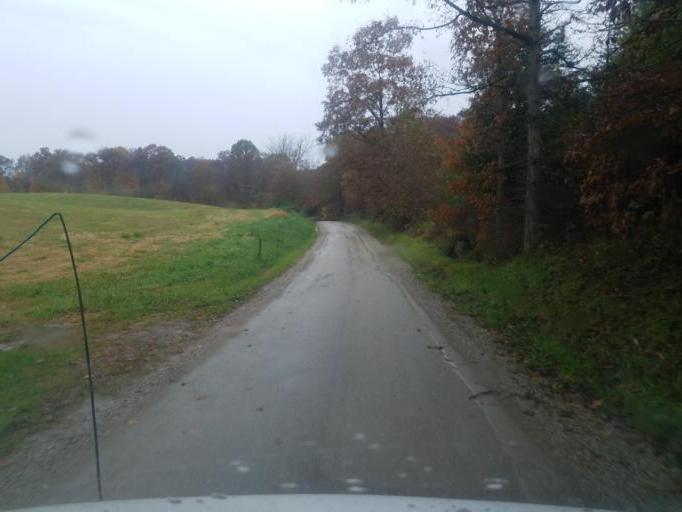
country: US
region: Ohio
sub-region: Washington County
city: Beverly
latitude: 39.4674
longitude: -81.6609
